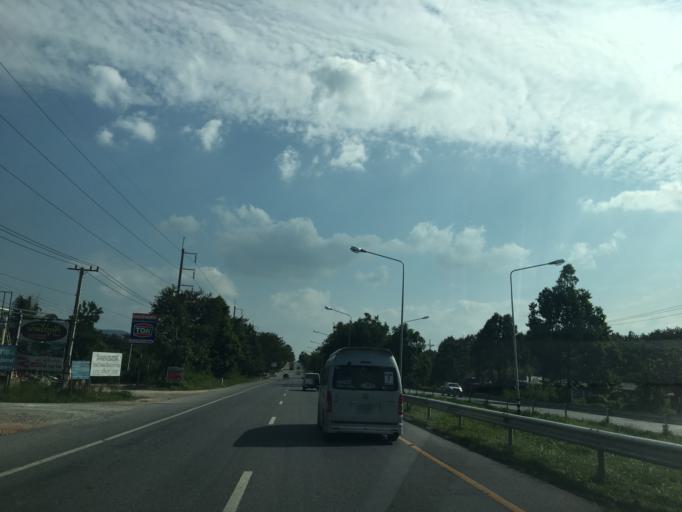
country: TH
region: Chiang Rai
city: Mae Lao
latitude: 19.7020
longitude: 99.7195
